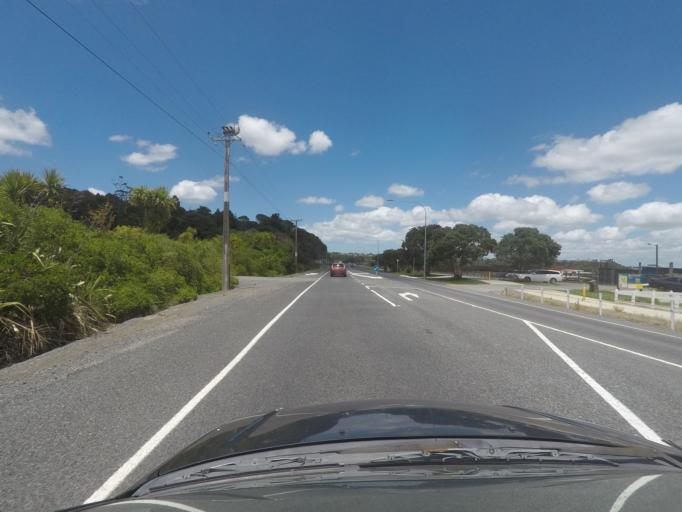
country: NZ
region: Northland
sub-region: Whangarei
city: Whangarei
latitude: -35.7345
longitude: 174.3497
